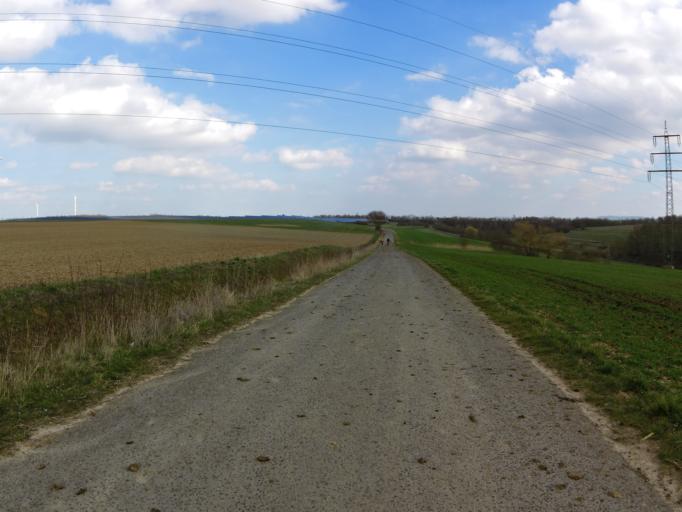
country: DE
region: Bavaria
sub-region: Regierungsbezirk Unterfranken
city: Biebelried
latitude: 49.7452
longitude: 10.0972
